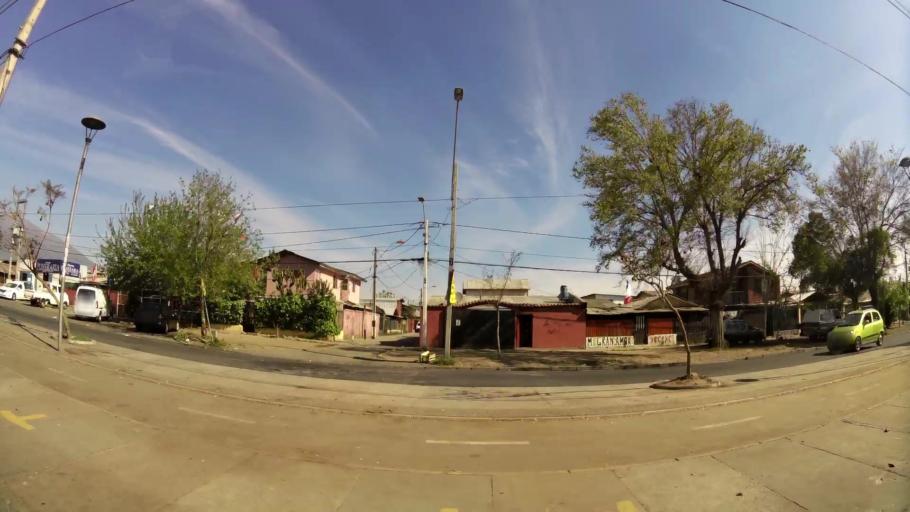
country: CL
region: Santiago Metropolitan
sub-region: Provincia de Santiago
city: Villa Presidente Frei, Nunoa, Santiago, Chile
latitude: -33.4770
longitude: -70.5697
